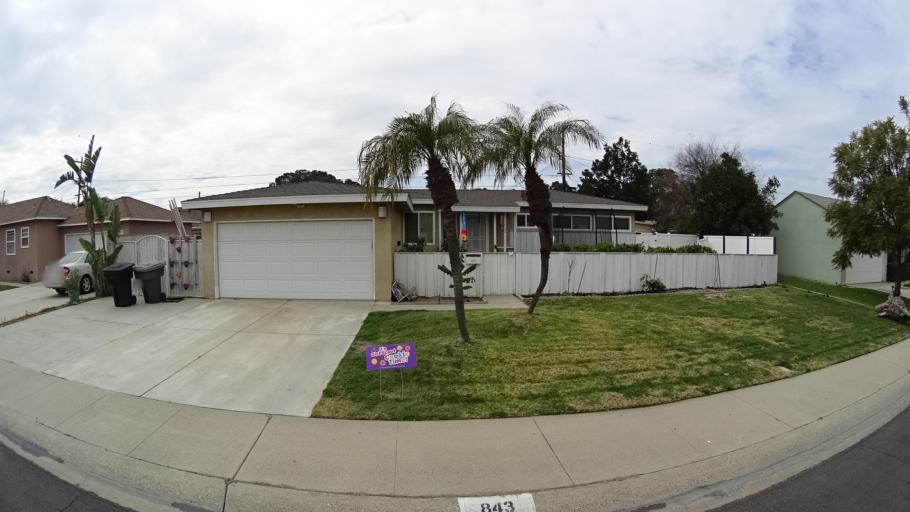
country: US
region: California
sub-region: Orange County
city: Anaheim
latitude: 33.8428
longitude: -117.9323
